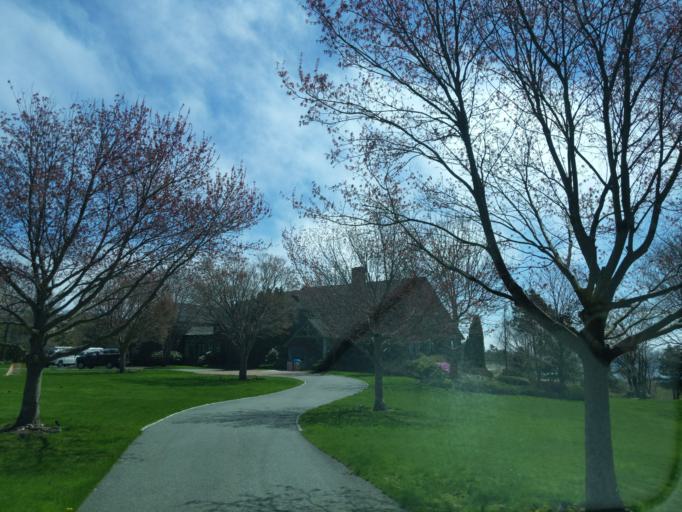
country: US
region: Massachusetts
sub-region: Essex County
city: Rockport
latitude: 42.6369
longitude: -70.6025
